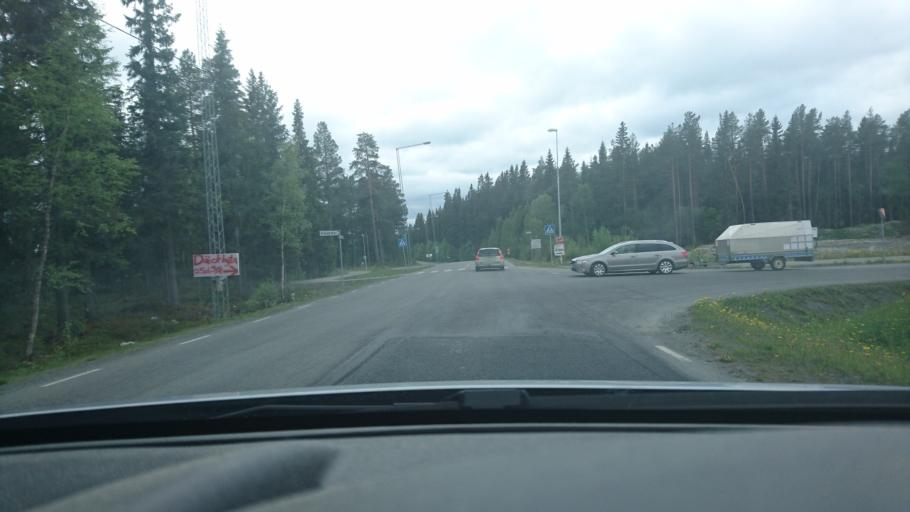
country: SE
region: Jaemtland
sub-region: OEstersunds Kommun
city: Ostersund
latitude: 63.1602
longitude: 14.7422
